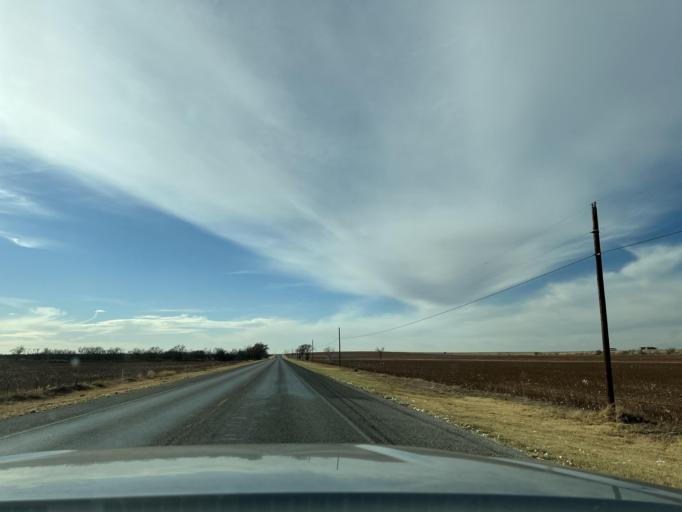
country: US
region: Texas
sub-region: Fisher County
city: Roby
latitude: 32.7409
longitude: -100.4766
